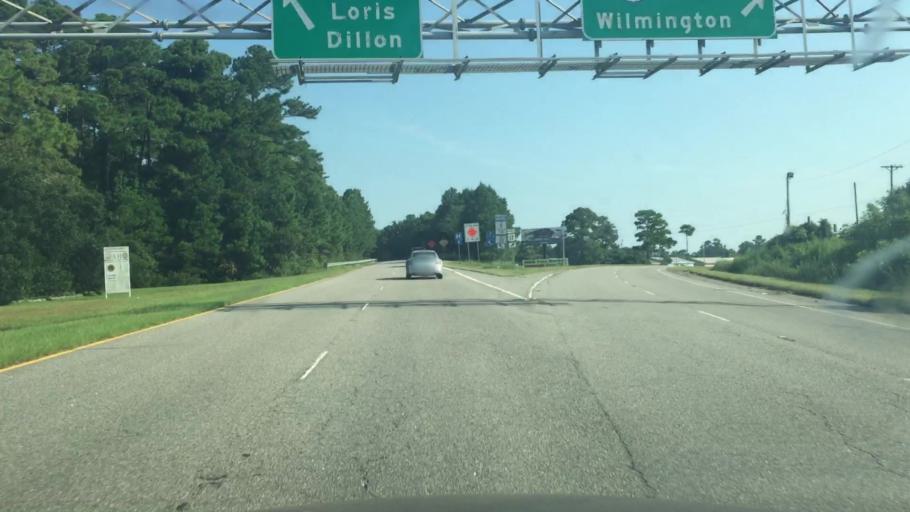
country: US
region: South Carolina
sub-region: Horry County
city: Little River
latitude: 33.8602
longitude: -78.6567
